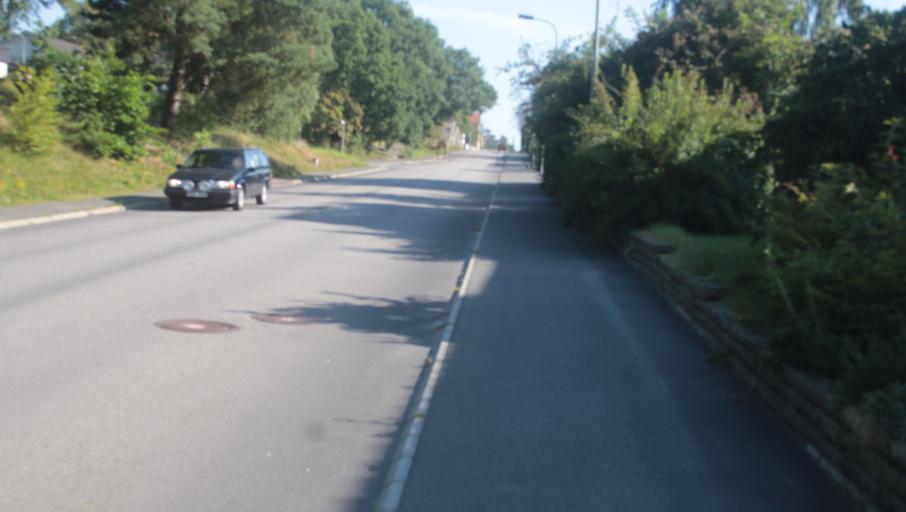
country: SE
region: Blekinge
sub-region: Karlshamns Kommun
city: Karlshamn
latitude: 56.1741
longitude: 14.8512
